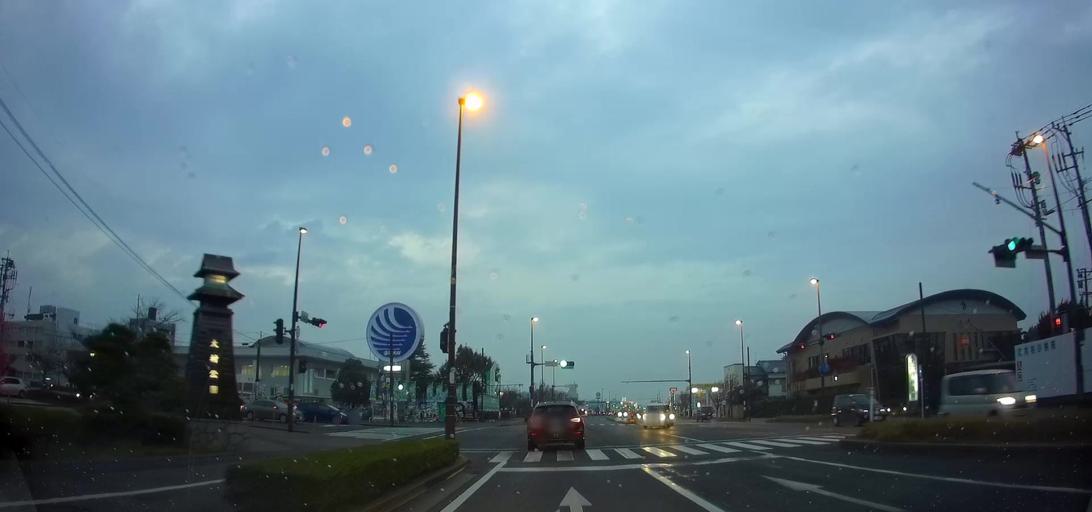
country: JP
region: Nagasaki
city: Omura
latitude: 32.8991
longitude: 129.9594
